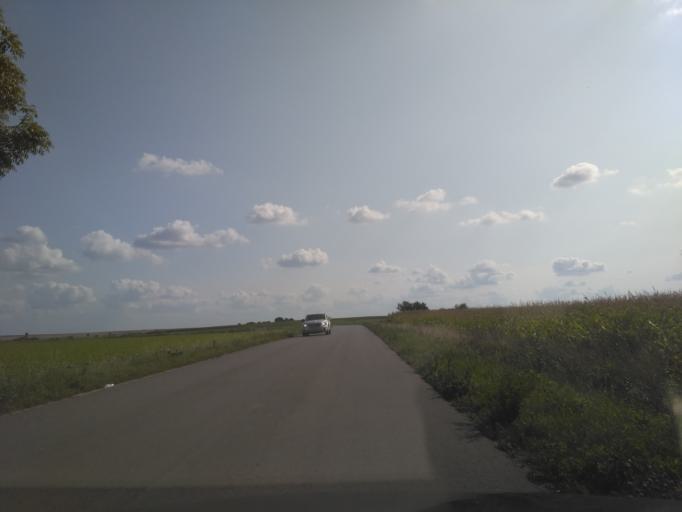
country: PL
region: Lublin Voivodeship
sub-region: Powiat chelmski
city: Pokrowka
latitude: 51.0778
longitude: 23.4732
